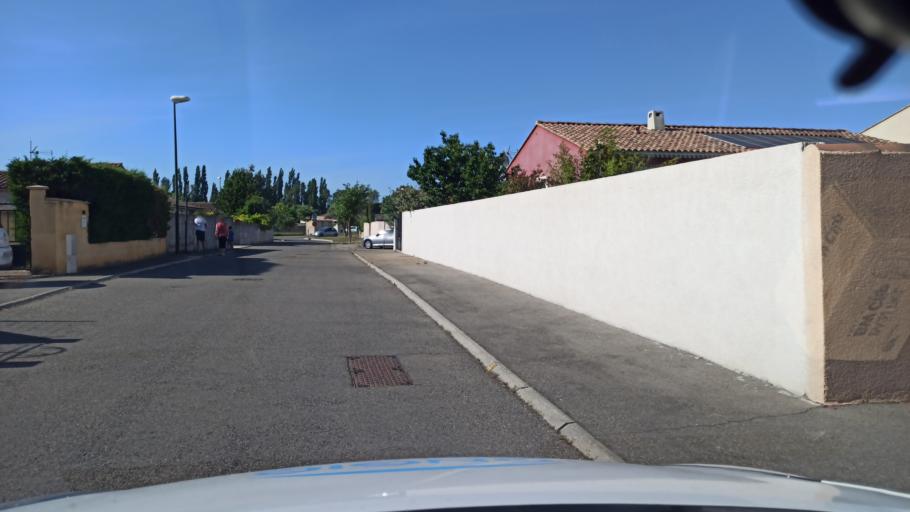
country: FR
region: Provence-Alpes-Cote d'Azur
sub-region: Departement du Vaucluse
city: Morieres-les-Avignon
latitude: 43.9554
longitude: 4.8929
